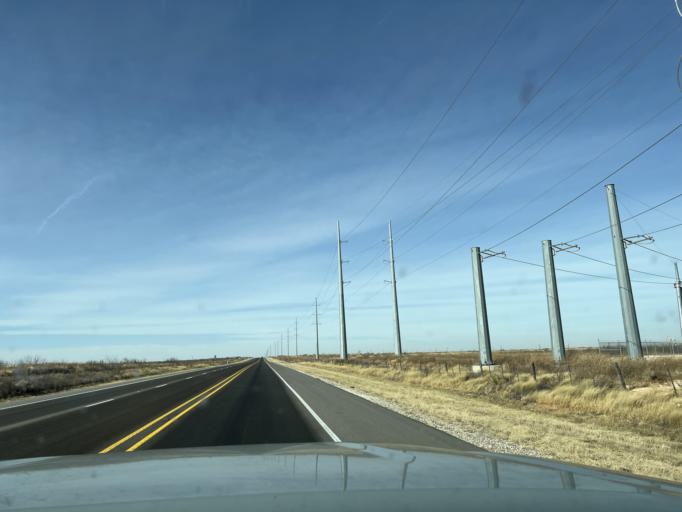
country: US
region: Texas
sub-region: Andrews County
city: Andrews
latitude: 32.3507
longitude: -102.7360
